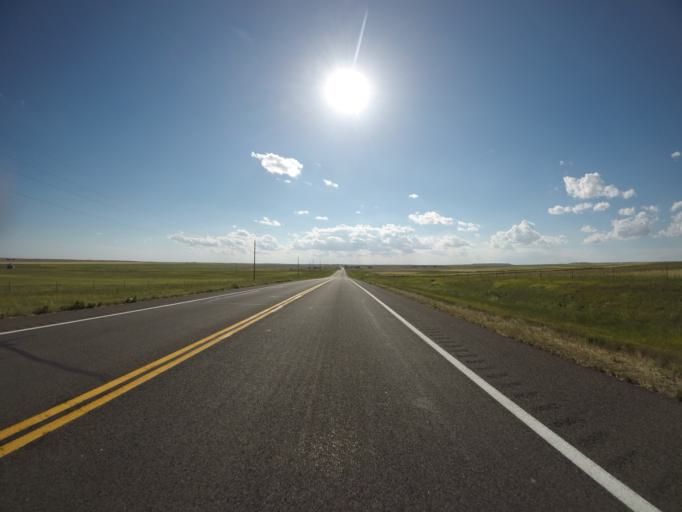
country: US
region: Colorado
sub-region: Morgan County
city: Fort Morgan
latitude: 40.6111
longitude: -103.7783
